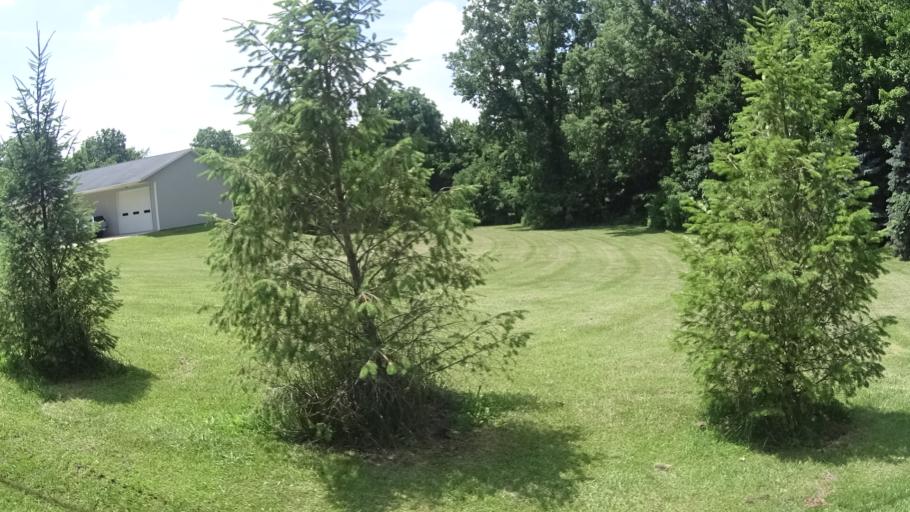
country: US
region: Ohio
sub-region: Erie County
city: Huron
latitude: 41.3157
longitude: -82.5204
